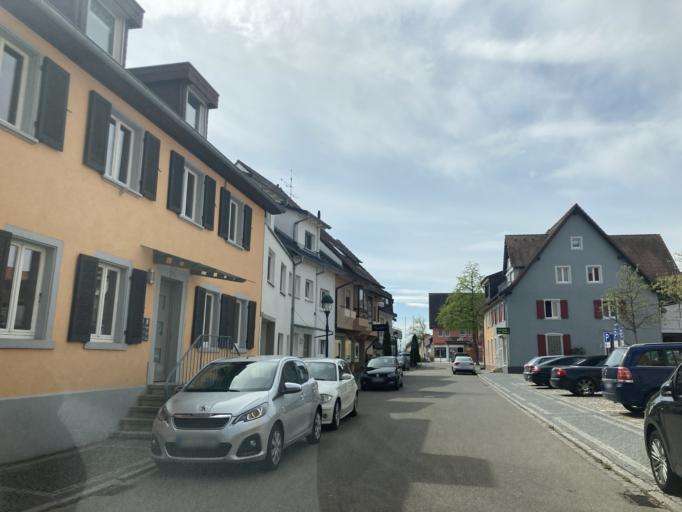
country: DE
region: Baden-Wuerttemberg
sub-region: Freiburg Region
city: Neuenburg am Rhein
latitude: 47.8145
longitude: 7.5624
